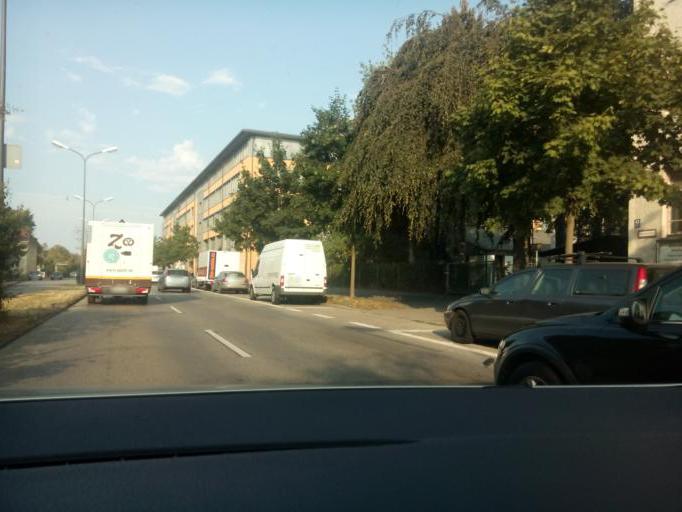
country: DE
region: Bavaria
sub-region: Upper Bavaria
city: Unterhaching
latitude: 48.1044
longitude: 11.6042
